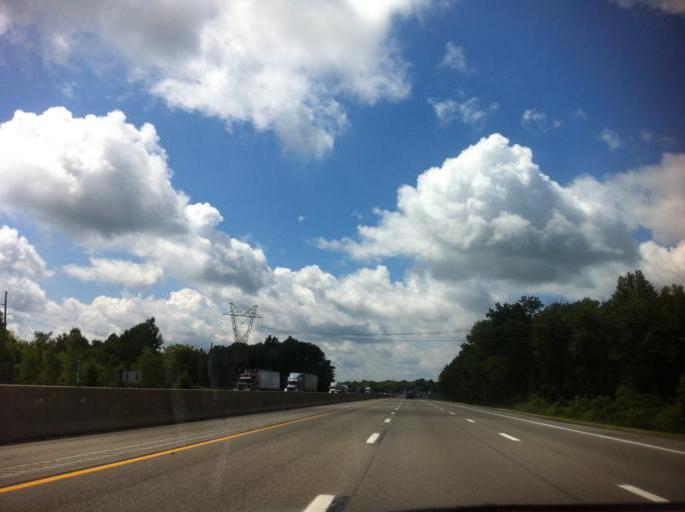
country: US
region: Ohio
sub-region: Lorain County
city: South Amherst
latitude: 41.3724
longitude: -82.2675
